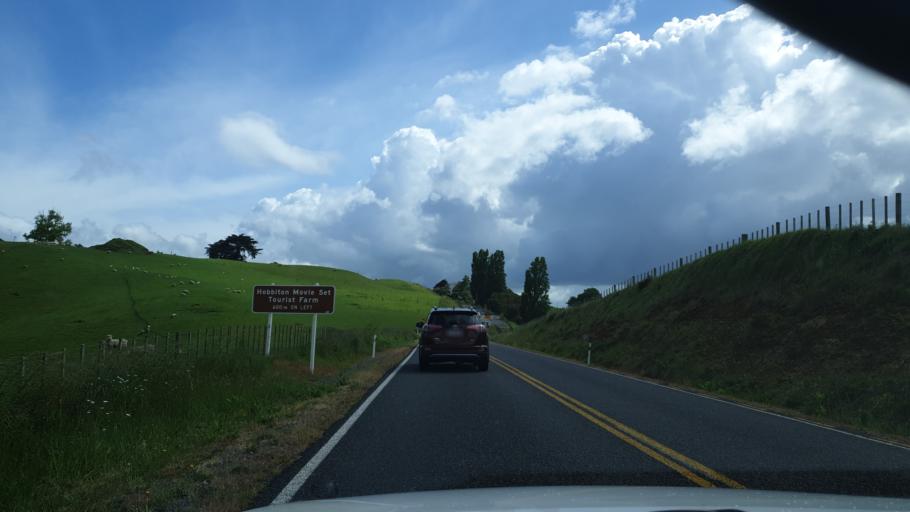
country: NZ
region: Waikato
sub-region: Matamata-Piako District
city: Matamata
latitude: -37.8747
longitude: 175.6855
